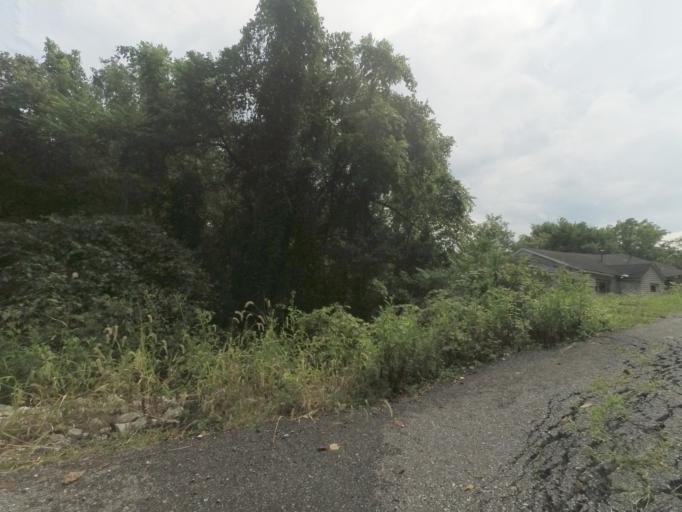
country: US
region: West Virginia
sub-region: Cabell County
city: Huntington
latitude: 38.4023
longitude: -82.4687
